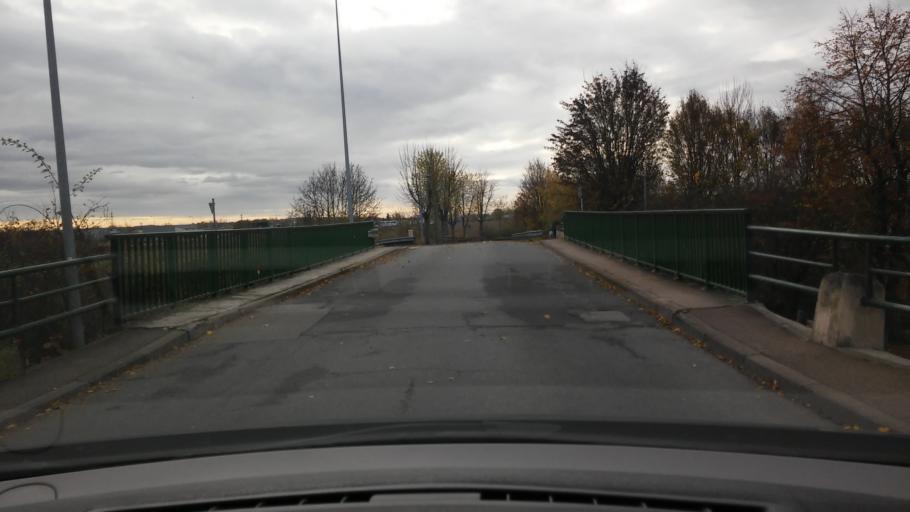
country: FR
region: Lorraine
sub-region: Departement de la Moselle
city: Talange
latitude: 49.2323
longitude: 6.1767
